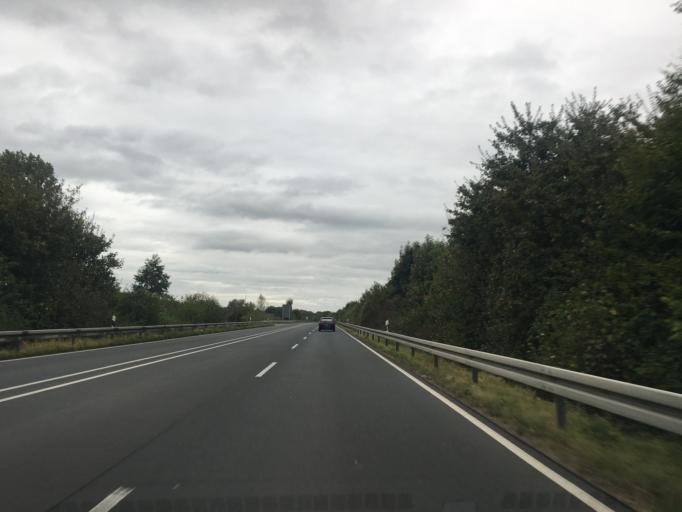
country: DE
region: North Rhine-Westphalia
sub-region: Regierungsbezirk Munster
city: Ochtrup
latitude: 52.1926
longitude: 7.2045
